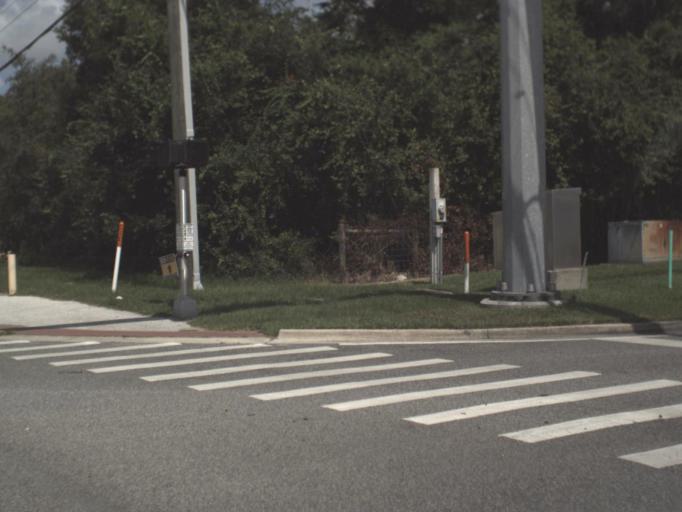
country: US
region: Florida
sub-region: Pasco County
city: Shady Hills
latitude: 28.3308
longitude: -82.5591
